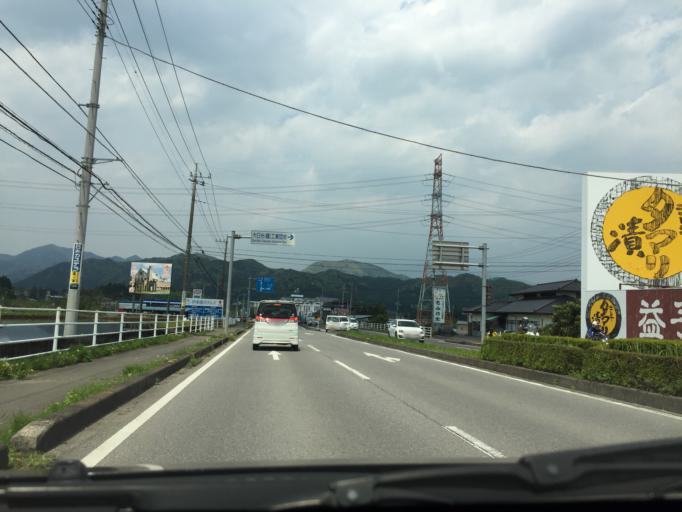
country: JP
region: Tochigi
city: Imaichi
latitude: 36.7642
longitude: 139.7167
